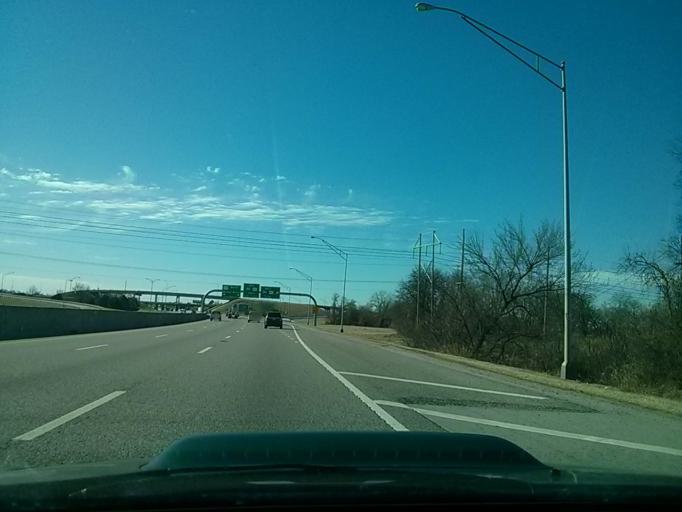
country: US
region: Oklahoma
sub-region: Tulsa County
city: Owasso
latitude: 36.1708
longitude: -95.8601
